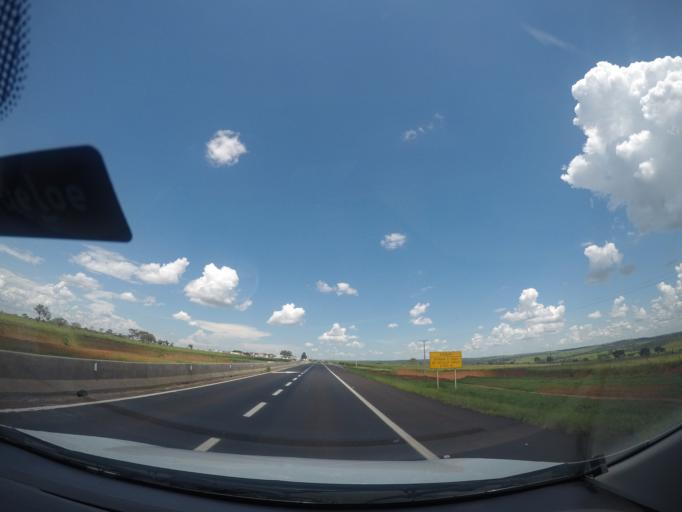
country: BR
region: Minas Gerais
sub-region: Prata
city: Prata
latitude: -19.4787
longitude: -48.8662
